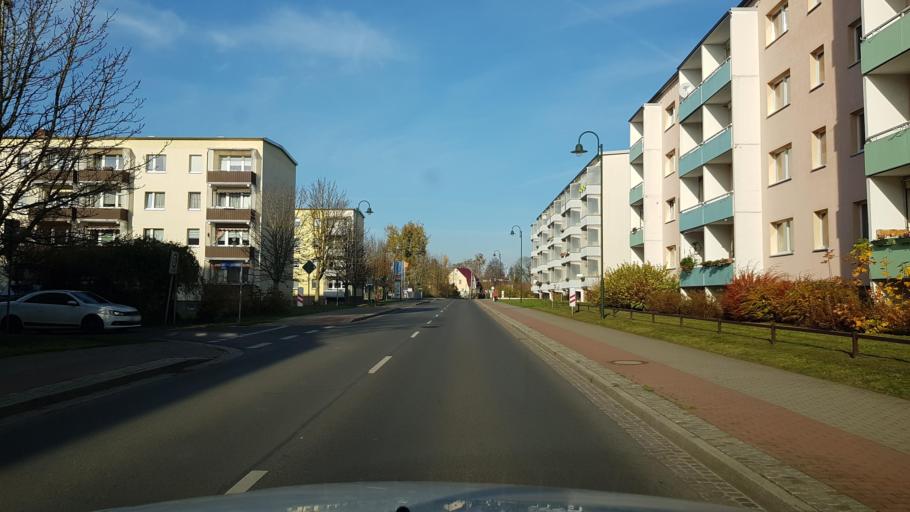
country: DE
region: Brandenburg
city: Brussow
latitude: 53.4549
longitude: 14.2104
